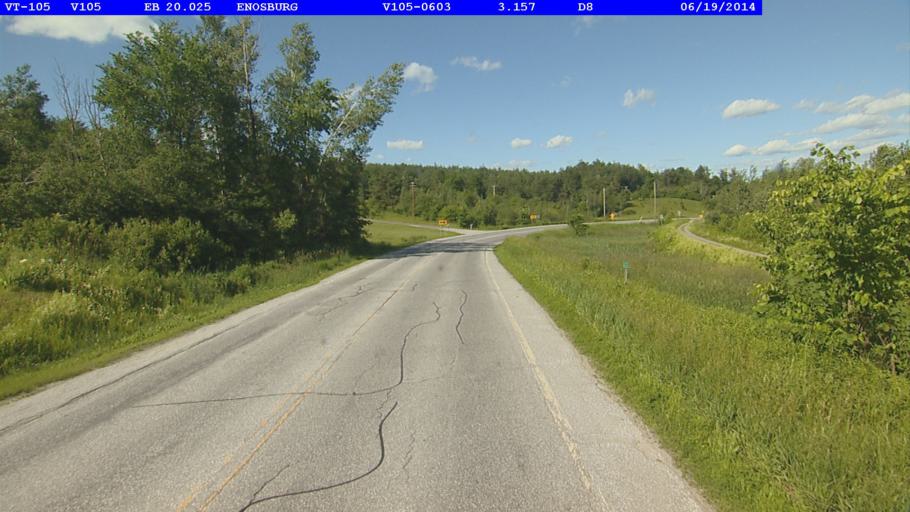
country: US
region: Vermont
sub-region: Franklin County
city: Enosburg Falls
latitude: 44.9203
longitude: -72.7651
